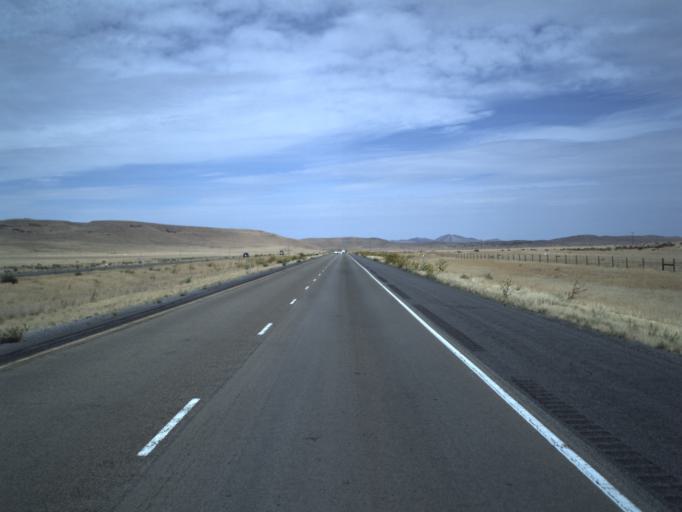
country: US
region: Utah
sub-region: Tooele County
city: Grantsville
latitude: 40.7934
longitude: -112.8370
